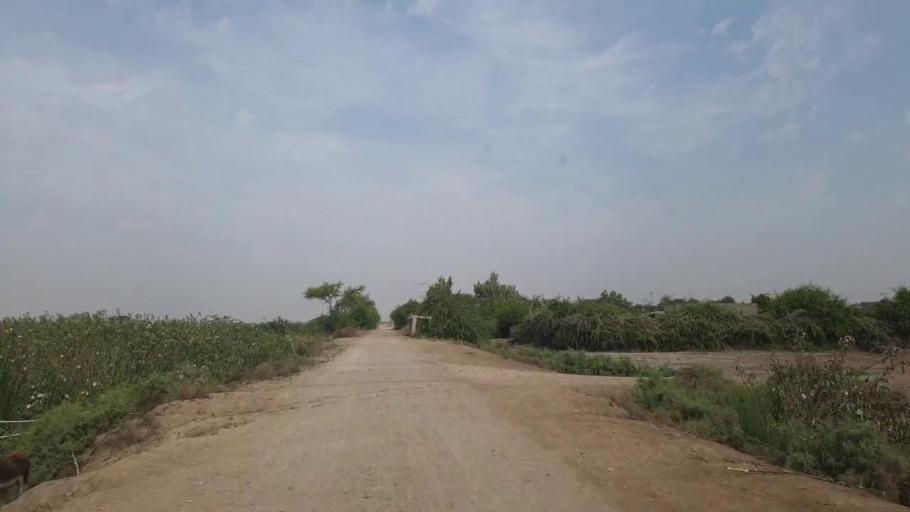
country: PK
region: Sindh
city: Rajo Khanani
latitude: 24.9878
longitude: 68.9951
